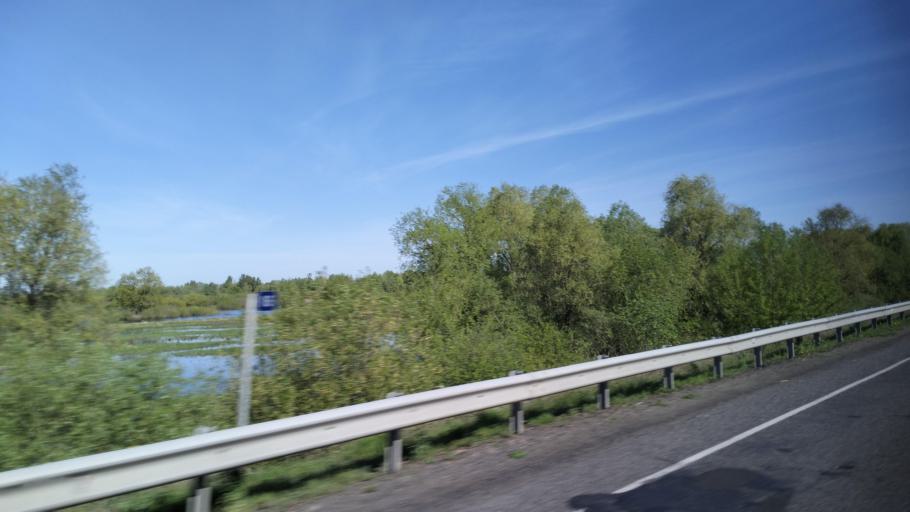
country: BY
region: Gomel
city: Turaw
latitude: 52.0896
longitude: 27.8284
